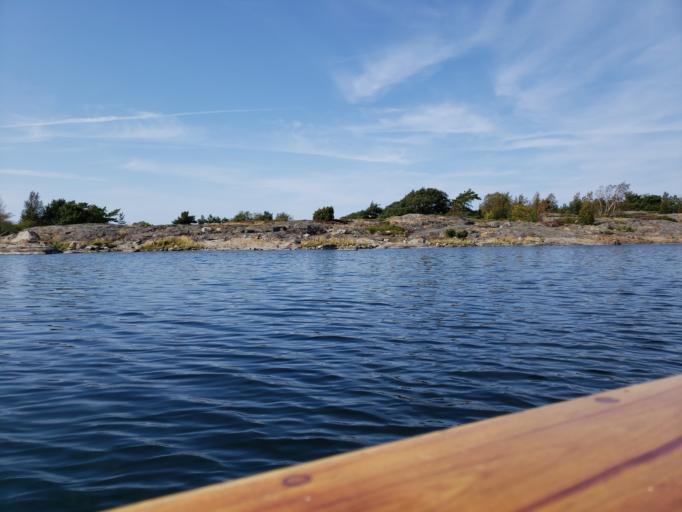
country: FI
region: Varsinais-Suomi
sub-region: Aboland-Turunmaa
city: Dragsfjaerd
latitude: 59.8477
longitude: 22.2076
